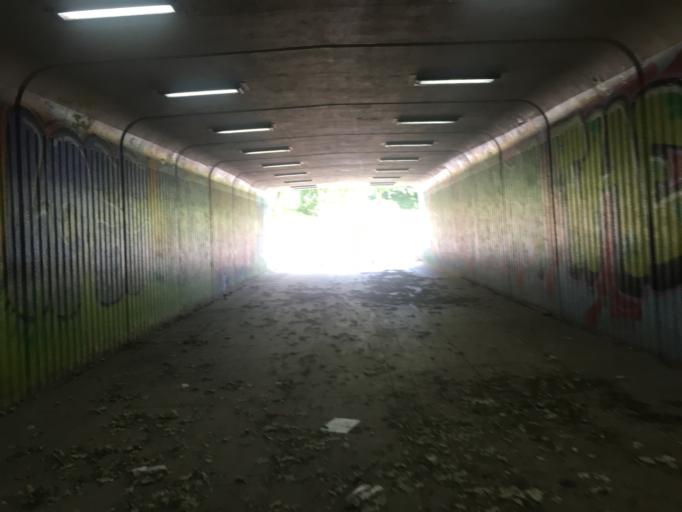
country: GB
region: England
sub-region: County Durham
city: Chester-le-Street
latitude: 54.8775
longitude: -1.5452
